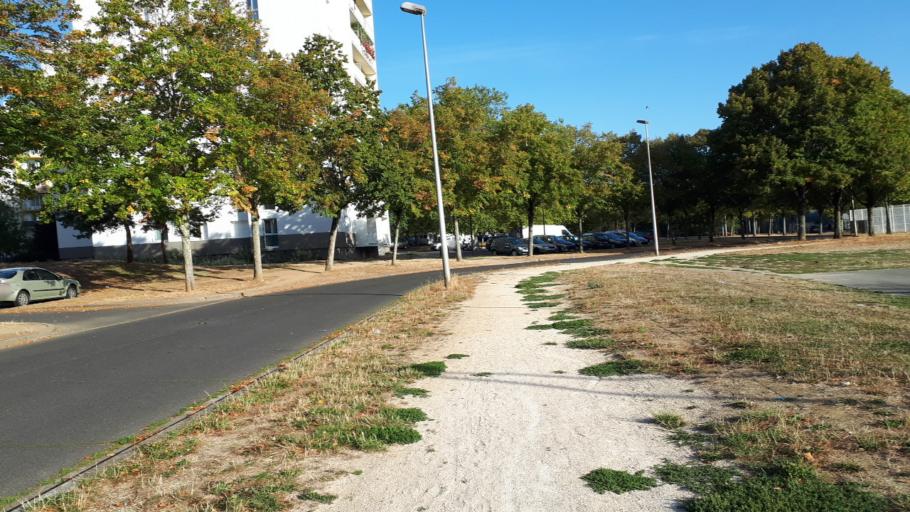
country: FR
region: Centre
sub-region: Departement du Loir-et-Cher
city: Blois
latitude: 47.5922
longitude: 1.3034
